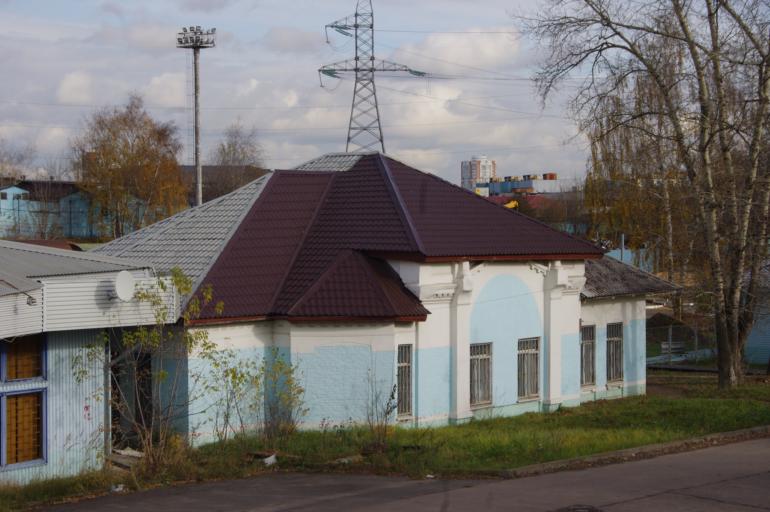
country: RU
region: Moscow
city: Novovladykino
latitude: 55.8469
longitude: 37.5908
